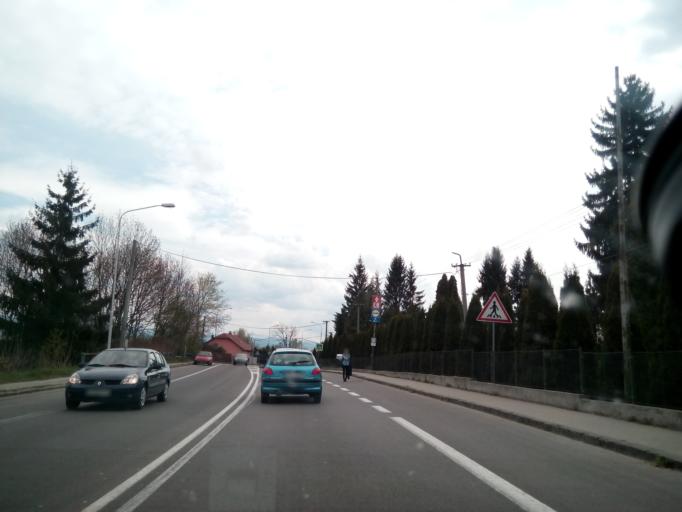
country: SK
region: Zilinsky
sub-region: Okres Zilina
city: Vrutky
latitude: 49.1099
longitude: 18.9167
